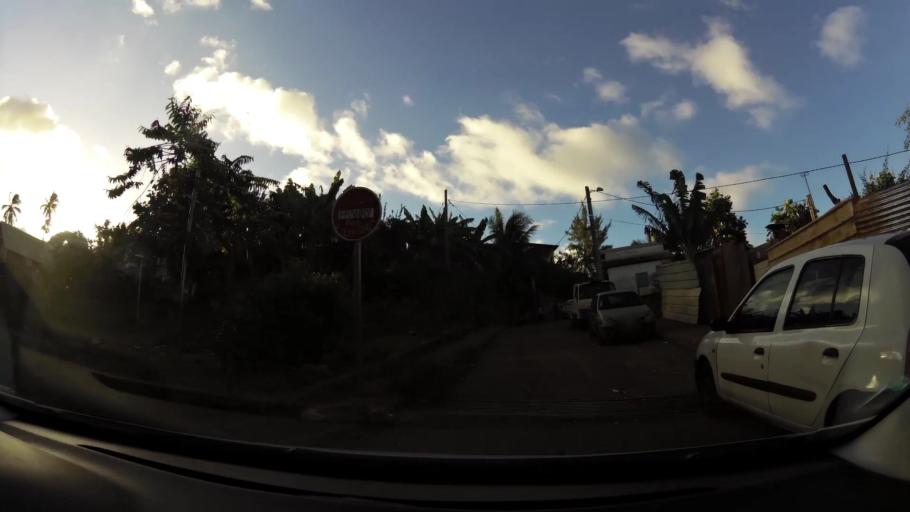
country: YT
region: Dembeni
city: Dembeni
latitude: -12.8166
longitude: 45.1978
